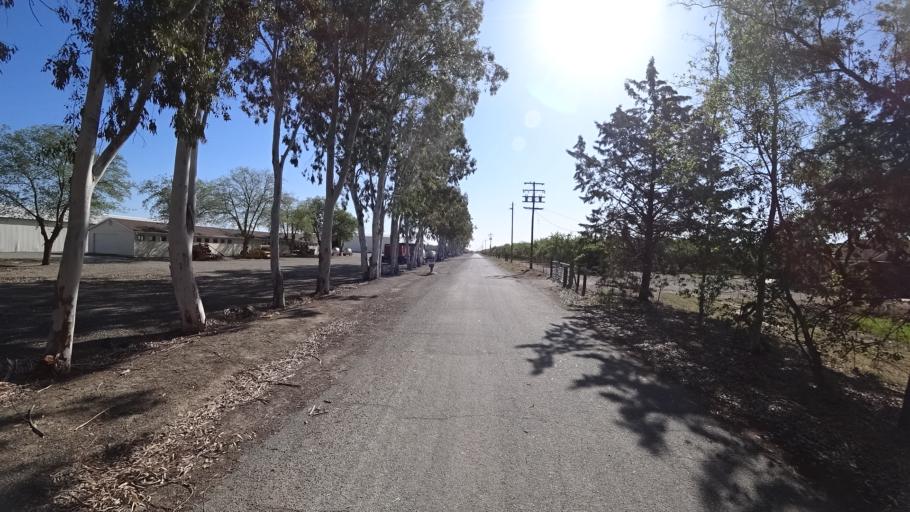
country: US
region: California
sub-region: Glenn County
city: Hamilton City
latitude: 39.6782
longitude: -122.0737
